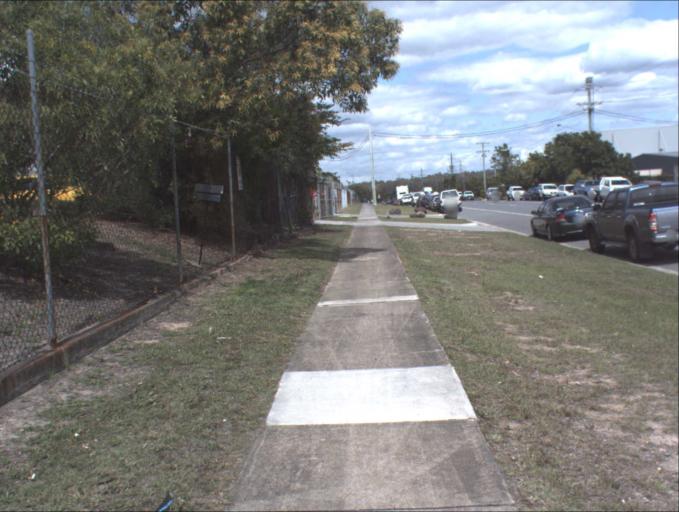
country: AU
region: Queensland
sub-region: Logan
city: Logan Reserve
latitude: -27.6833
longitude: 153.0706
